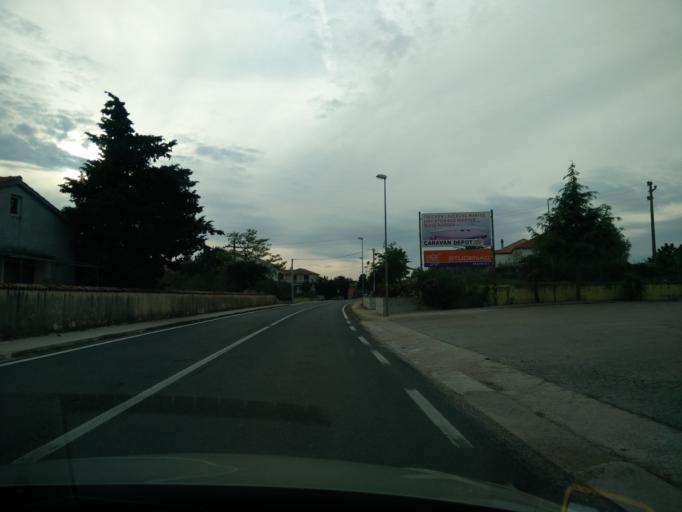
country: HR
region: Zadarska
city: Turanj
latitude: 43.9677
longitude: 15.4111
